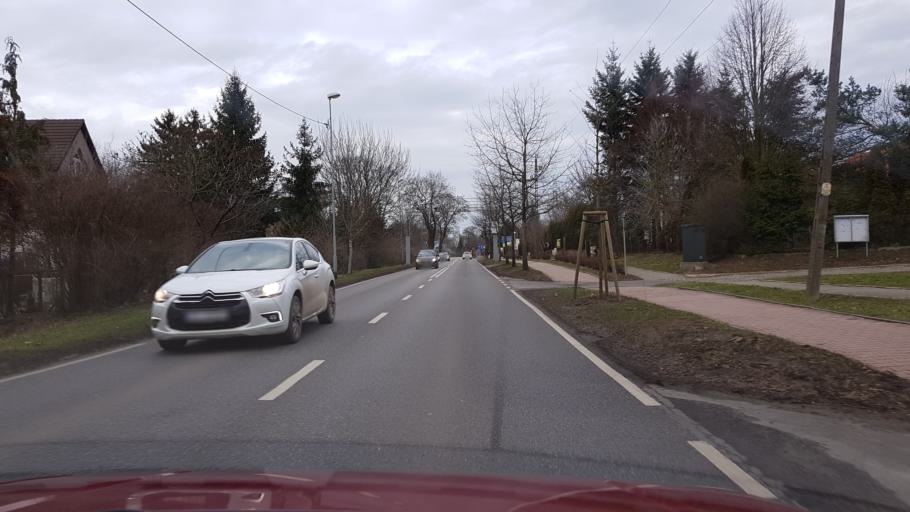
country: PL
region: West Pomeranian Voivodeship
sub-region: Powiat policki
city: Dobra
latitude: 53.4919
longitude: 14.4810
